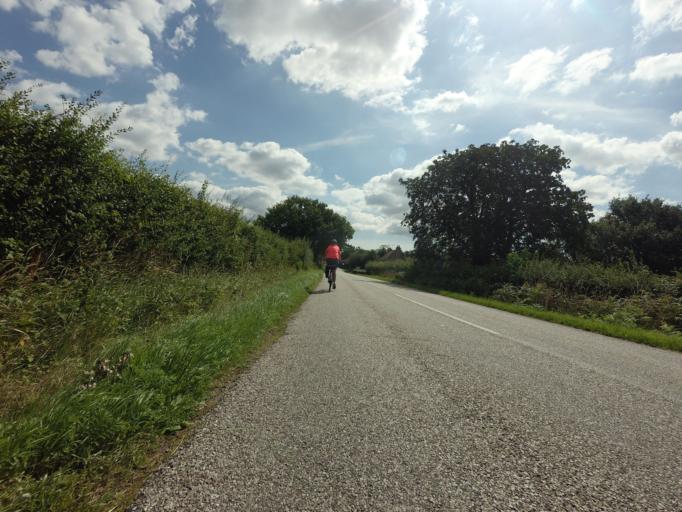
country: GB
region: England
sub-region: Kent
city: Tenterden
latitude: 51.0735
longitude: 0.7349
